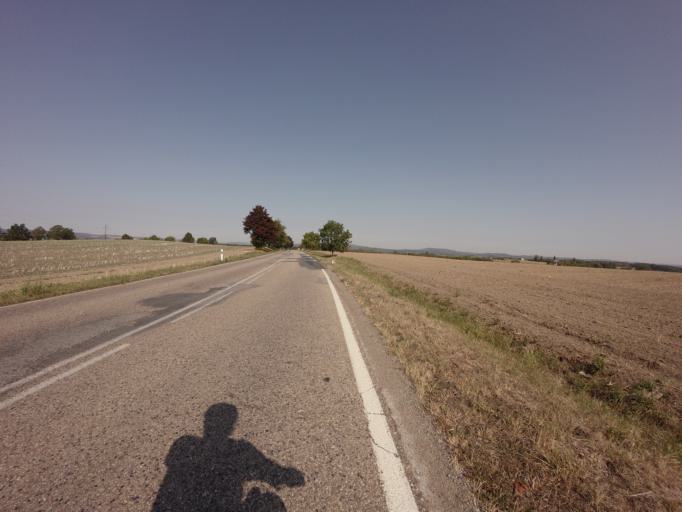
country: CZ
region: Central Bohemia
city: Porici nad Sazavou
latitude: 49.8086
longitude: 14.6488
